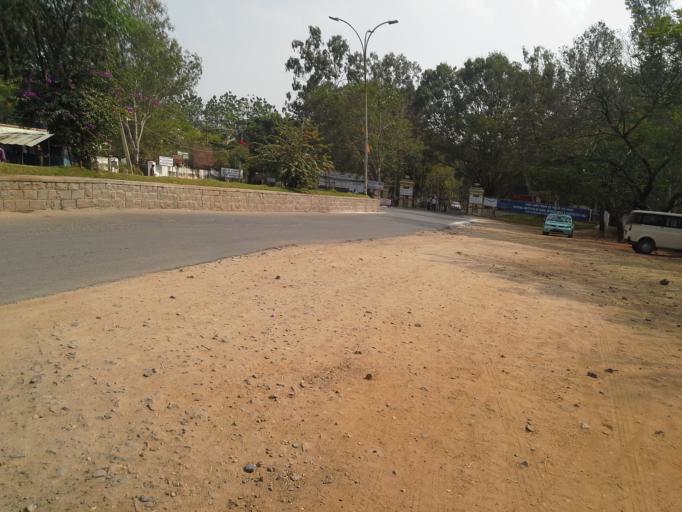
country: IN
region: Telangana
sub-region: Hyderabad
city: Hyderabad
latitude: 17.3171
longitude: 78.4038
